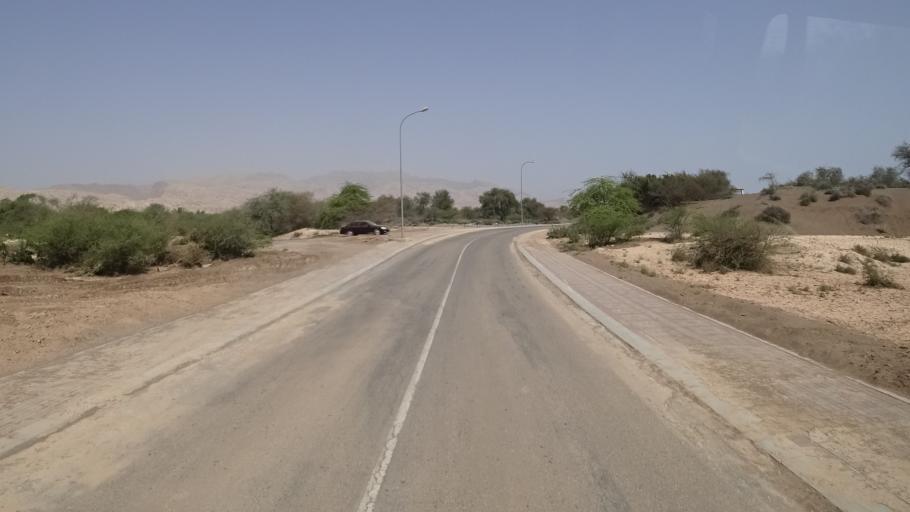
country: OM
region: Muhafazat Masqat
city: Muscat
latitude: 23.2356
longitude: 58.9103
